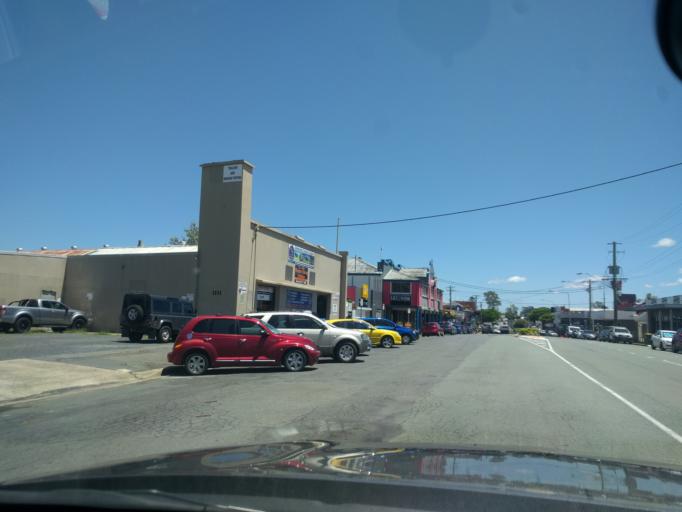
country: AU
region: Queensland
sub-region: Logan
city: Cedar Vale
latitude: -27.9896
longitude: 152.9960
